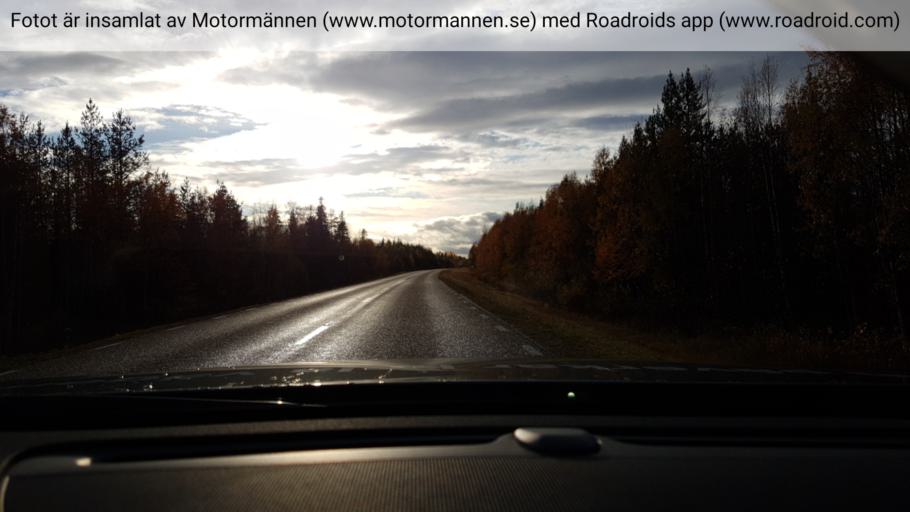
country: SE
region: Norrbotten
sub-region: Pajala Kommun
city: Pajala
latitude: 67.1687
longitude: 22.6677
